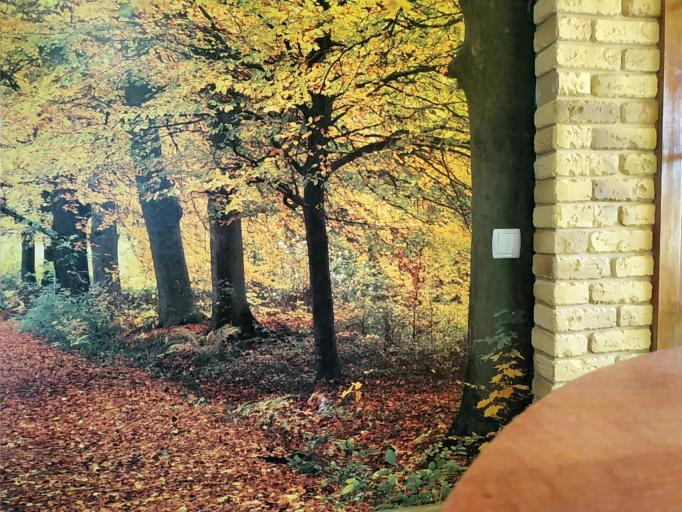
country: RU
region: Pskov
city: Dno
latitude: 57.9100
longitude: 30.1845
